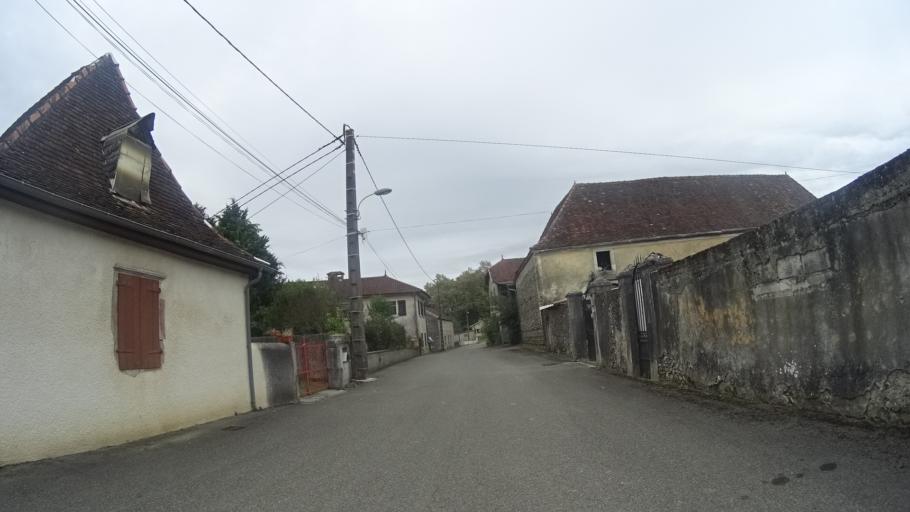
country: FR
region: Aquitaine
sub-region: Departement des Pyrenees-Atlantiques
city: Orthez
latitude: 43.4690
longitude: -0.7175
